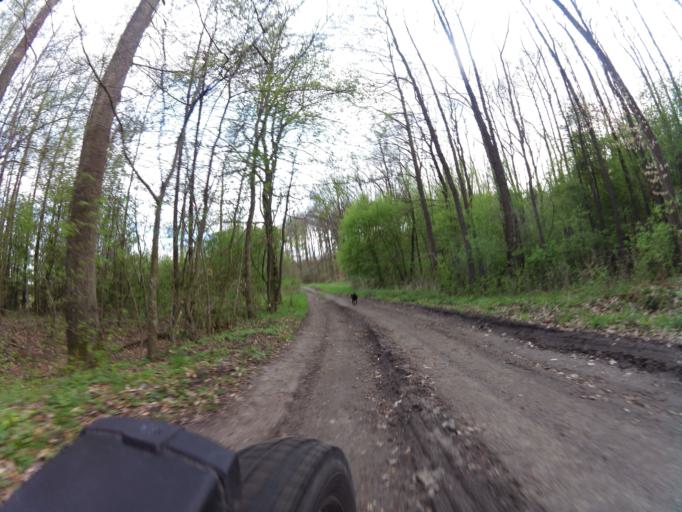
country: PL
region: West Pomeranian Voivodeship
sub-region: Powiat lobeski
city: Lobez
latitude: 53.7389
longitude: 15.6326
